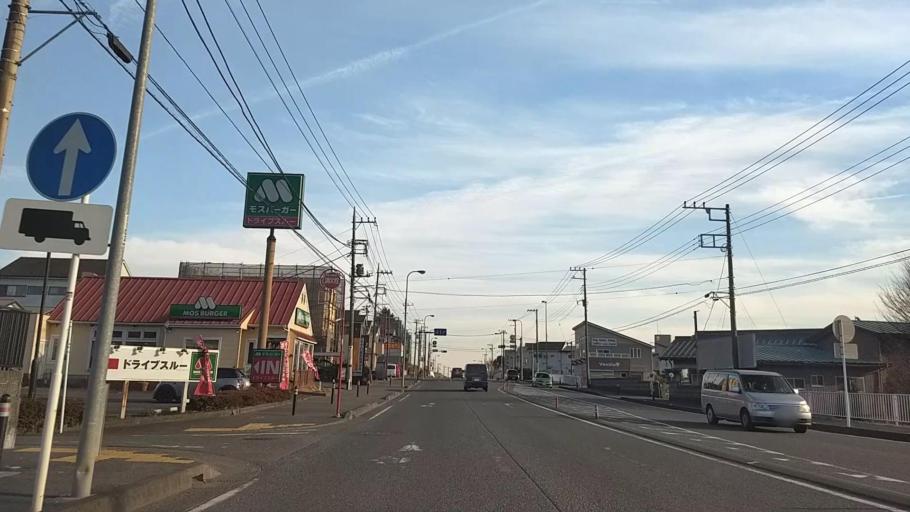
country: JP
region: Kanagawa
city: Atsugi
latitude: 35.4935
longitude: 139.3190
